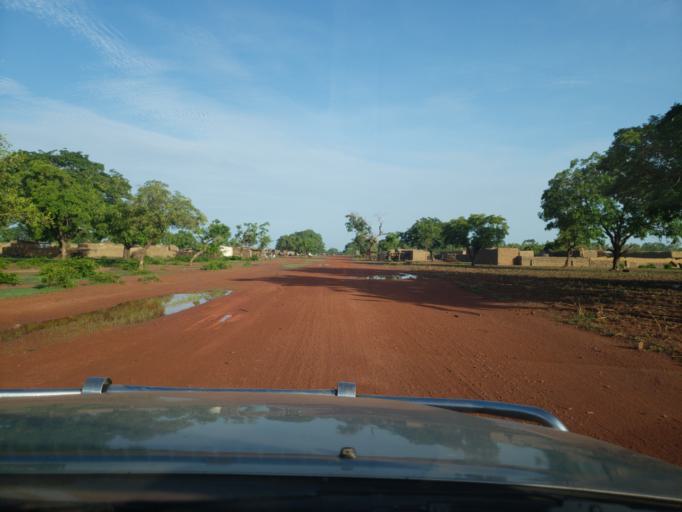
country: ML
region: Sikasso
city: Koutiala
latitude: 12.4182
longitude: -5.5760
